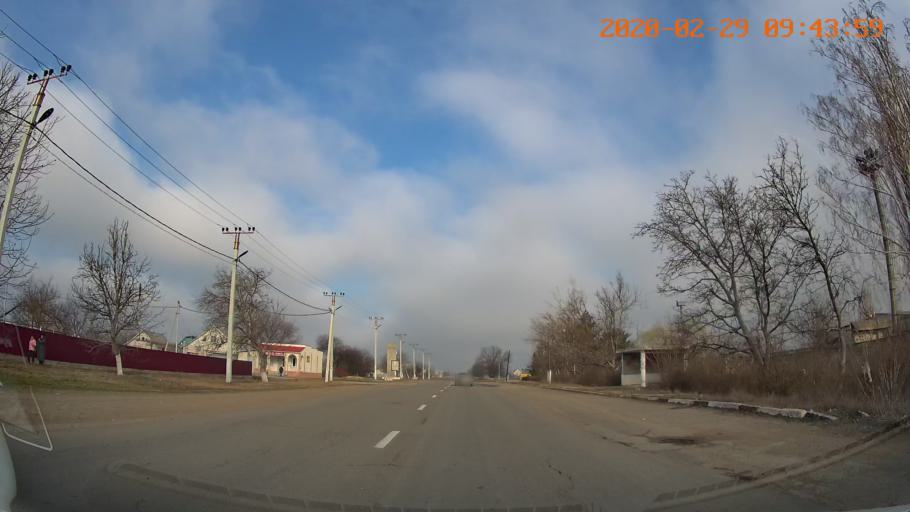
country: MD
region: Telenesti
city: Crasnoe
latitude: 46.6488
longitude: 29.8188
